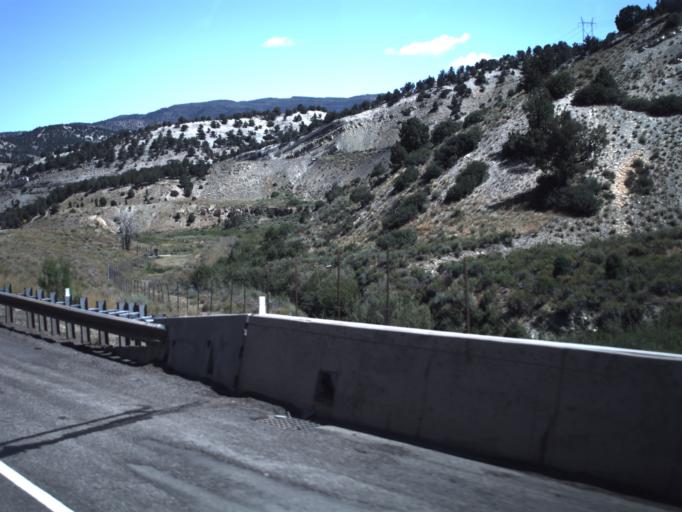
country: US
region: Utah
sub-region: Sanpete County
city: Fairview
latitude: 39.9331
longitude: -111.1999
